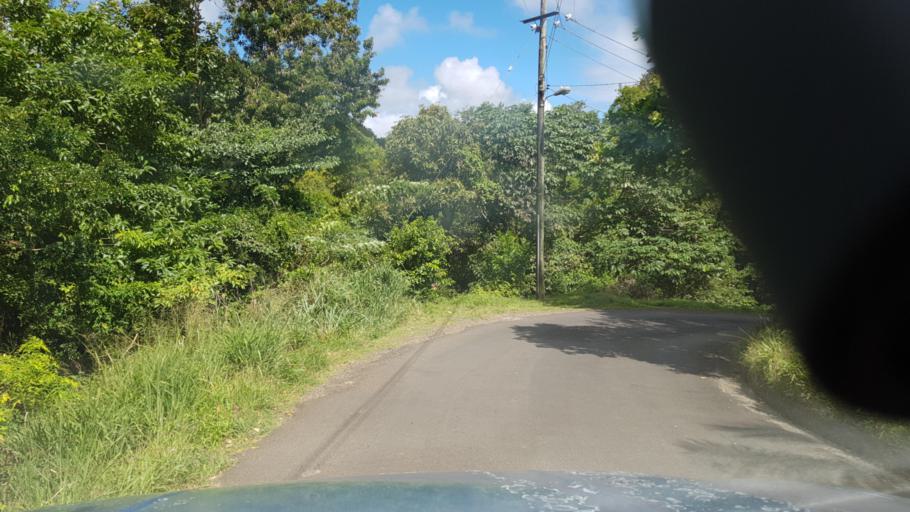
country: LC
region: Gros-Islet
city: Gros Islet
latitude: 14.0465
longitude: -60.9494
